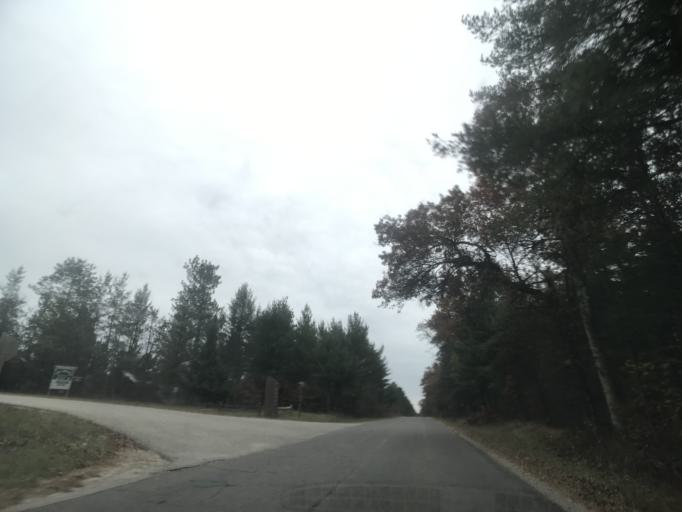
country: US
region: Wisconsin
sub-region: Oconto County
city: Gillett
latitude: 45.2590
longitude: -88.2521
